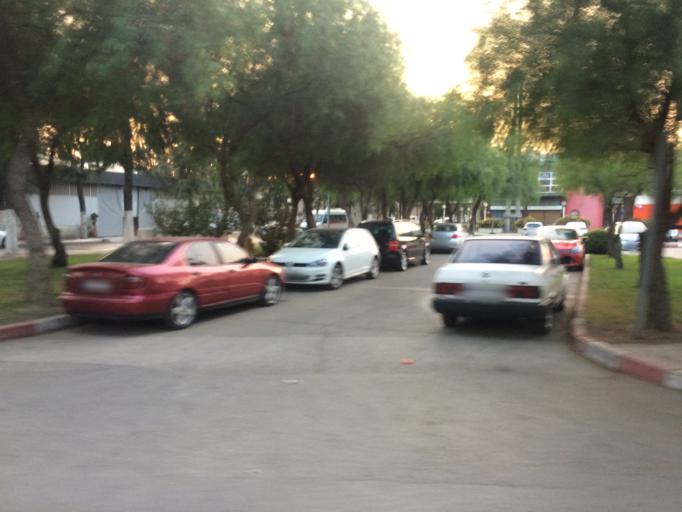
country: TR
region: Izmir
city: Karsiyaka
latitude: 38.4974
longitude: 27.0447
